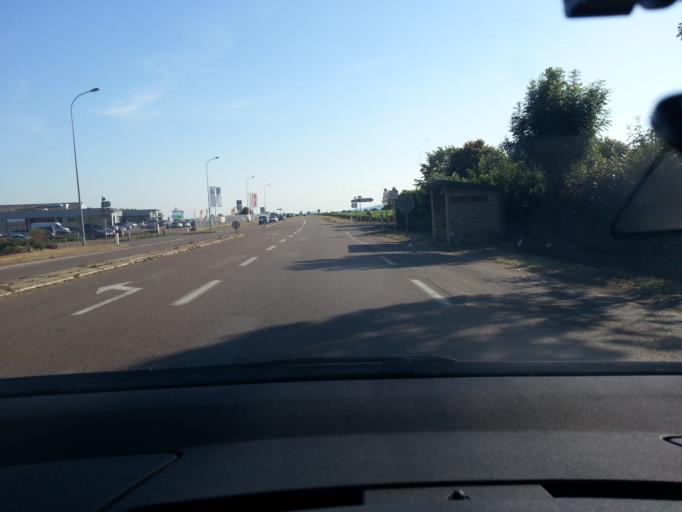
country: FR
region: Bourgogne
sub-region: Departement de la Cote-d'Or
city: Beaune
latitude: 47.0647
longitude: 4.8677
